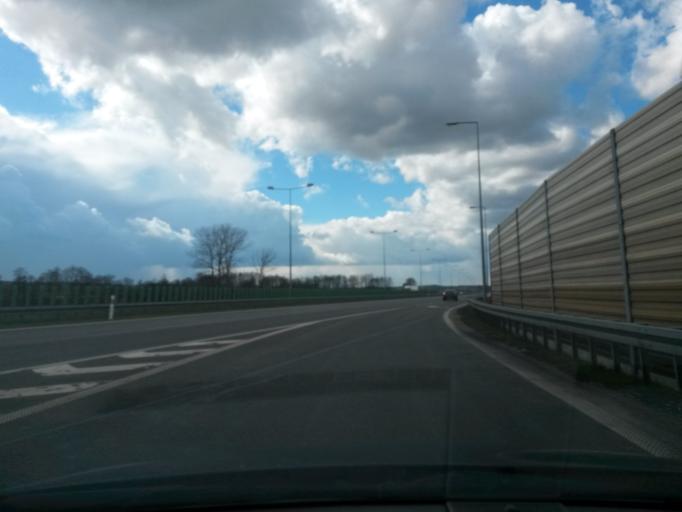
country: PL
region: Greater Poland Voivodeship
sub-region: Powiat turecki
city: Brudzew
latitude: 52.1361
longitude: 18.6313
